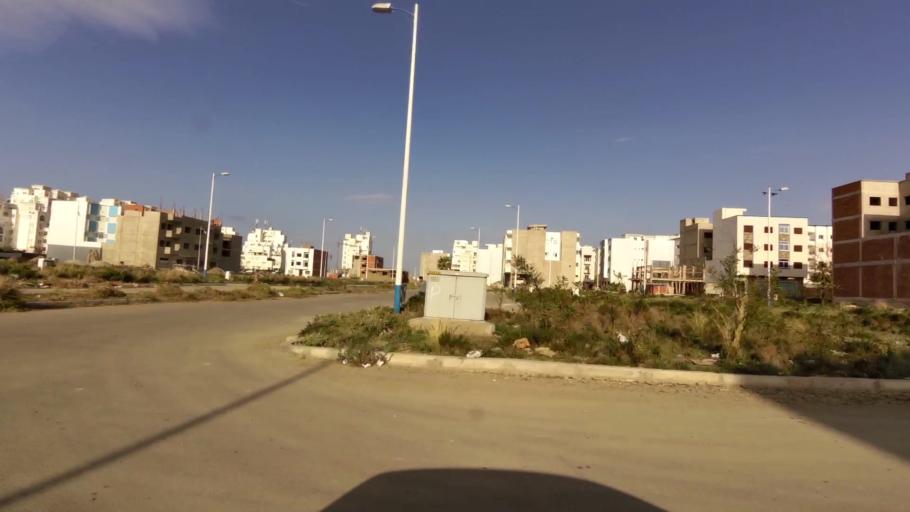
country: MA
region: Tanger-Tetouan
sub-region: Tetouan
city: Martil
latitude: 35.6295
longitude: -5.2782
